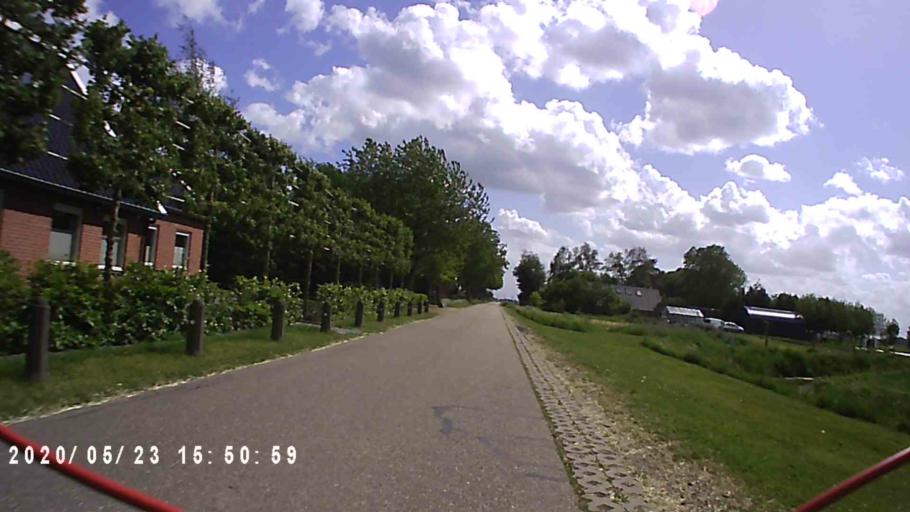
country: NL
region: Groningen
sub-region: Gemeente Delfzijl
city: Delfzijl
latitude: 53.2726
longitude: 6.9048
